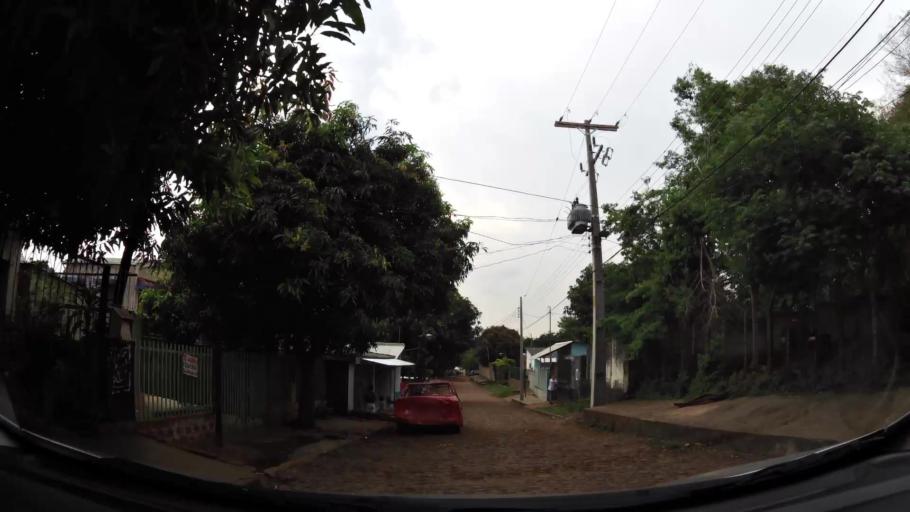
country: PY
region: Alto Parana
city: Presidente Franco
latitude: -25.5446
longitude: -54.6117
